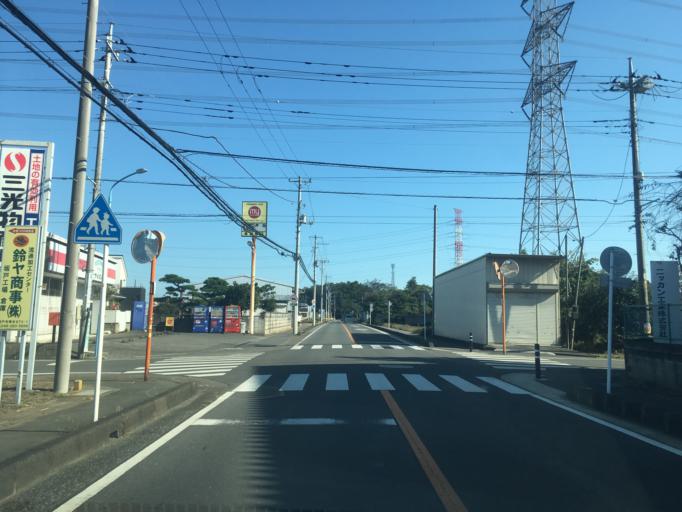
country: JP
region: Saitama
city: Sakado
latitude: 35.9657
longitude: 139.4354
